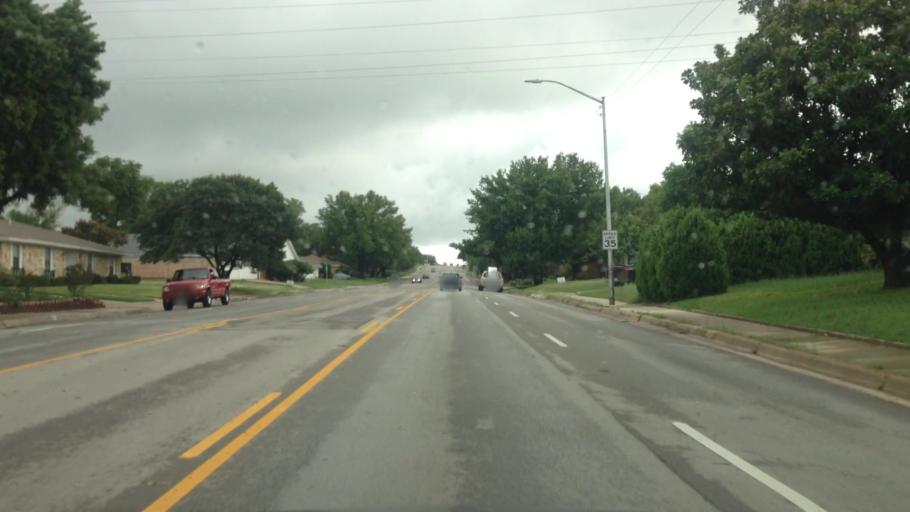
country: US
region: Texas
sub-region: Tarrant County
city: Edgecliff Village
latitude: 32.6532
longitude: -97.3959
